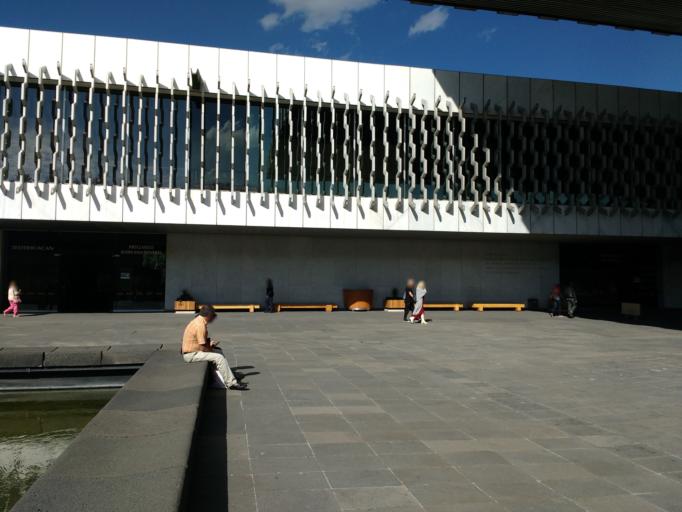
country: MX
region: Mexico City
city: Polanco
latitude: 19.4261
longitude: -99.1865
